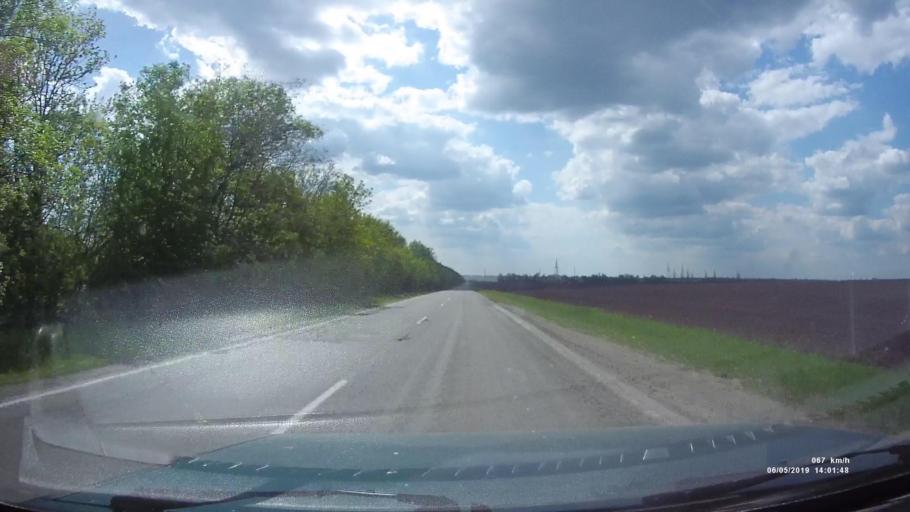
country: RU
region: Rostov
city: Shakhty
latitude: 47.6840
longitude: 40.3736
